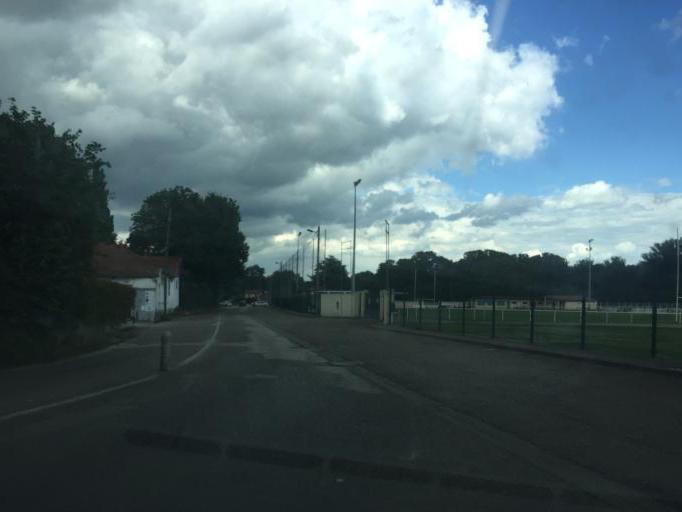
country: FR
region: Rhone-Alpes
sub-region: Departement de l'Isere
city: Pont-de-Cheruy
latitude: 45.7641
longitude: 5.1798
